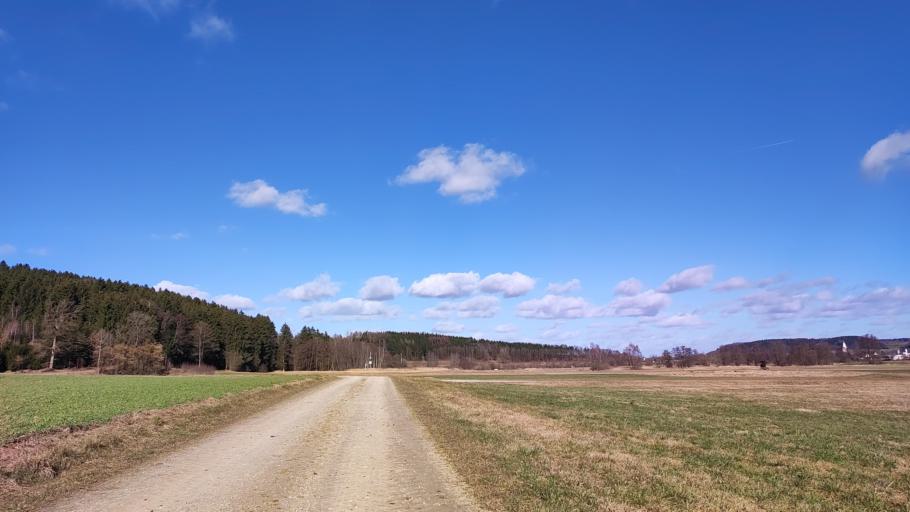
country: DE
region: Bavaria
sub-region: Swabia
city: Zusmarshausen
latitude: 48.4255
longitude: 10.5899
